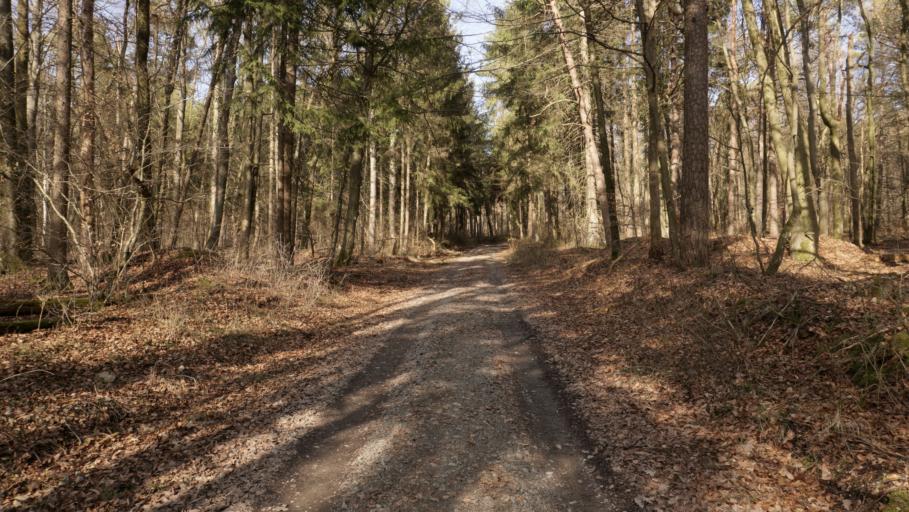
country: DE
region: Baden-Wuerttemberg
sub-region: Karlsruhe Region
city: Mosbach
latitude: 49.3870
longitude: 9.1686
